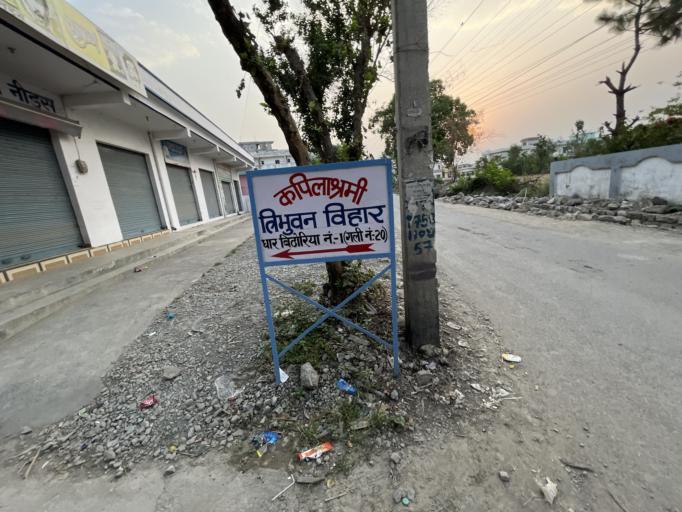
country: IN
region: Uttarakhand
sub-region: Naini Tal
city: Haldwani
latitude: 29.2301
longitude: 79.5047
